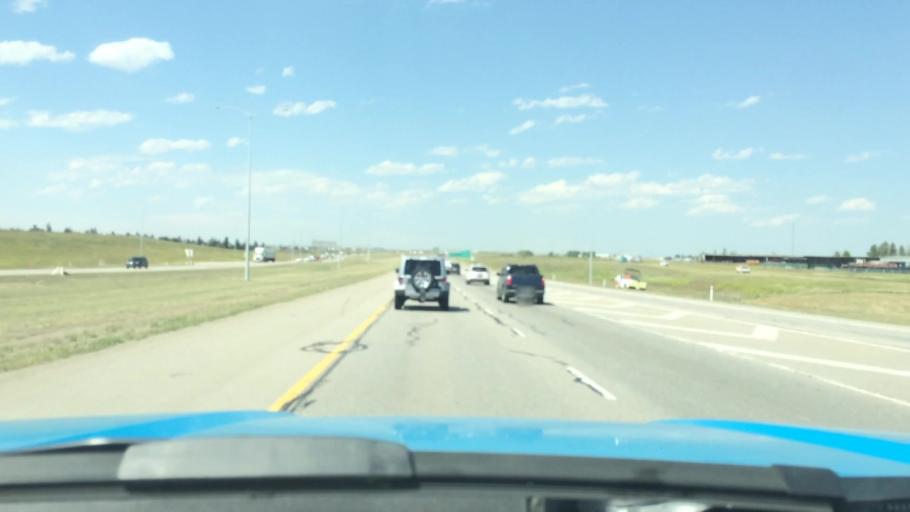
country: CA
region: Alberta
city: Chestermere
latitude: 51.0710
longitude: -113.9202
